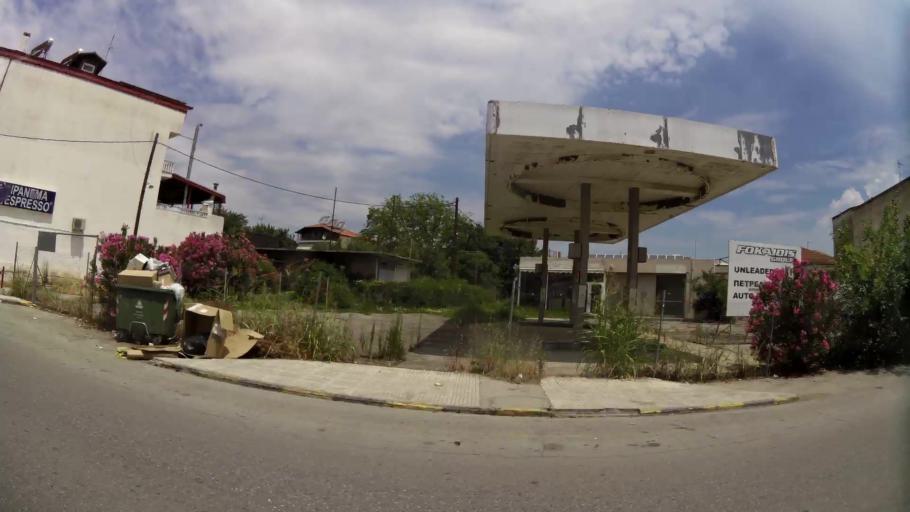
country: GR
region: Central Macedonia
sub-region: Nomos Pierias
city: Katerini
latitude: 40.2685
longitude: 22.5192
